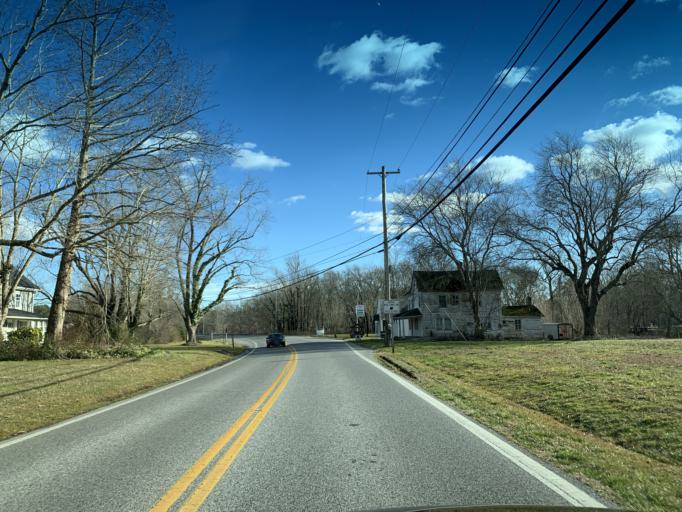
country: US
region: Maryland
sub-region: Worcester County
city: Berlin
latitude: 38.3150
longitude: -75.1942
